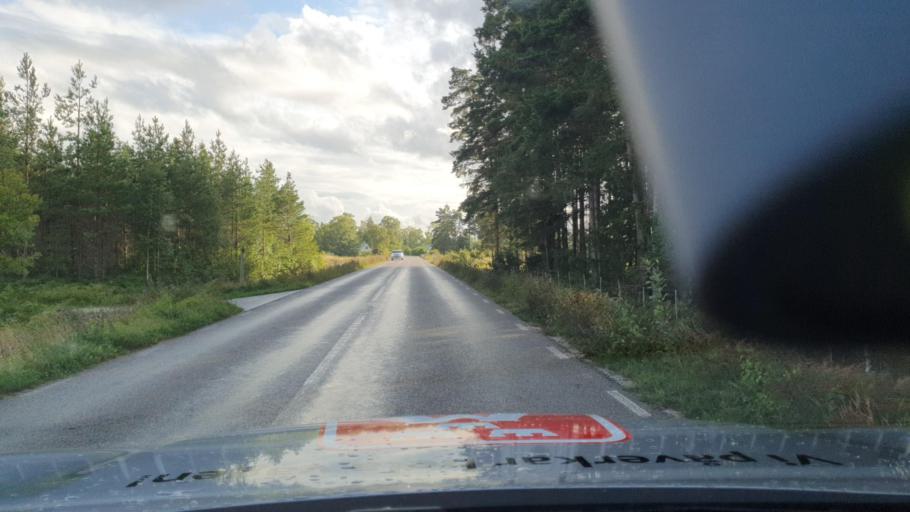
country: SE
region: Gotland
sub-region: Gotland
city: Slite
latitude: 57.6569
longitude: 18.7704
